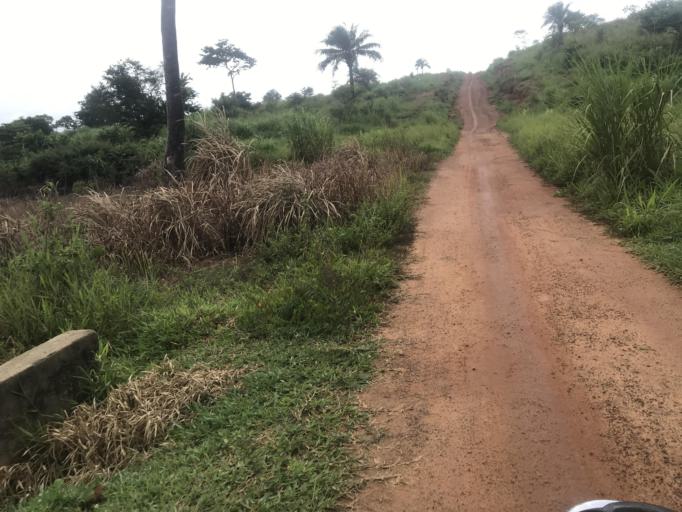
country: GN
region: Nzerekore
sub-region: Prefecture de Guekedou
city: Gueckedou
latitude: 8.4771
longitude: -10.2925
